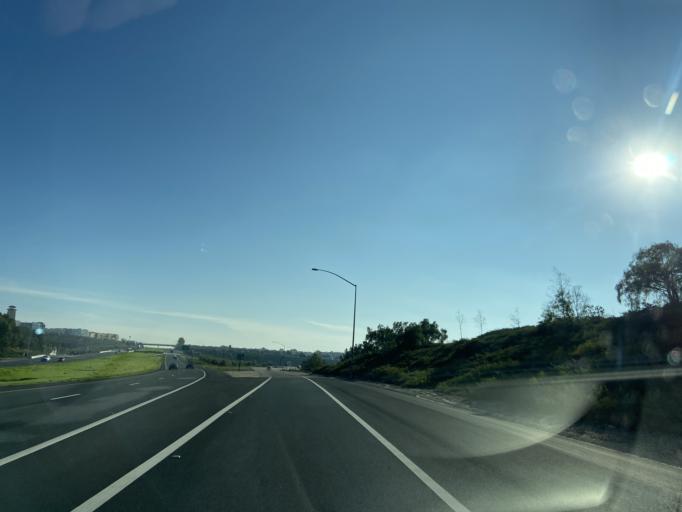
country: US
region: California
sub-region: San Diego County
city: Bonita
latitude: 32.6369
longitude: -116.9716
